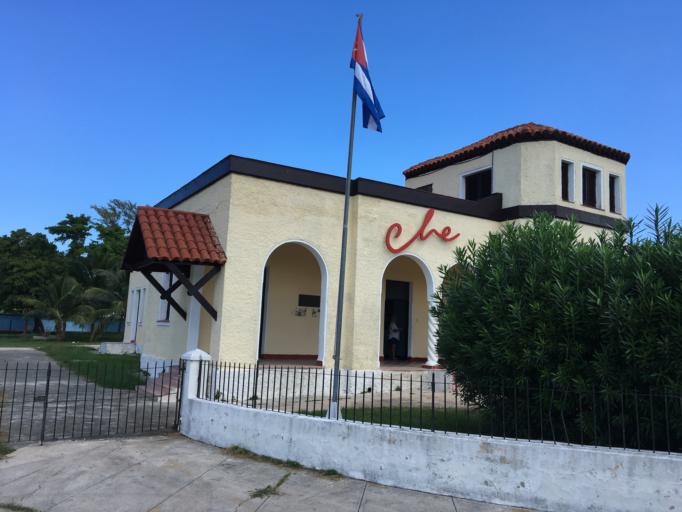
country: CU
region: La Habana
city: La Habana Vieja
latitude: 23.1442
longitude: -82.3455
